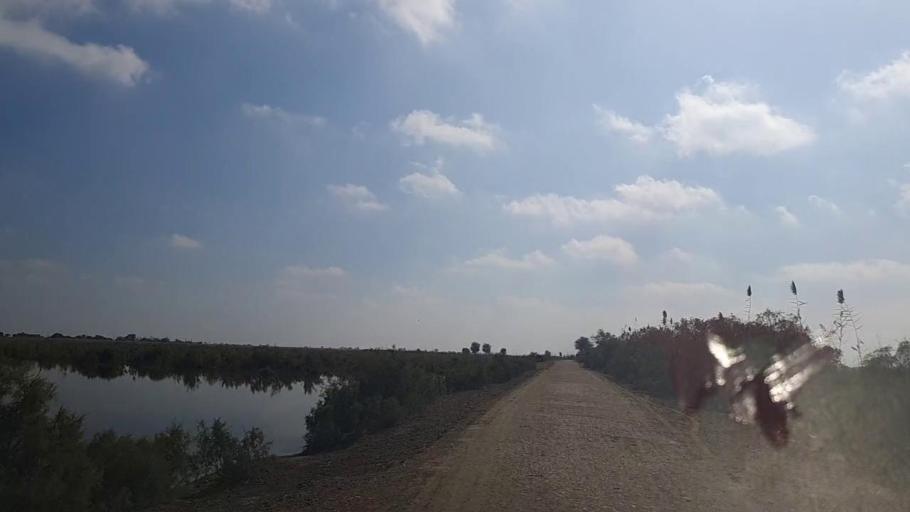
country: PK
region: Sindh
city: Sanghar
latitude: 26.0632
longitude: 69.0049
